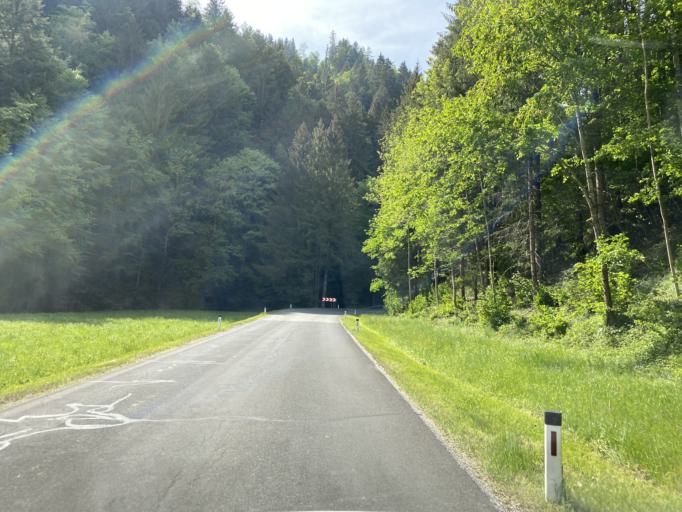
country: AT
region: Styria
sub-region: Politischer Bezirk Weiz
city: Koglhof
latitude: 47.3072
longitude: 15.6599
